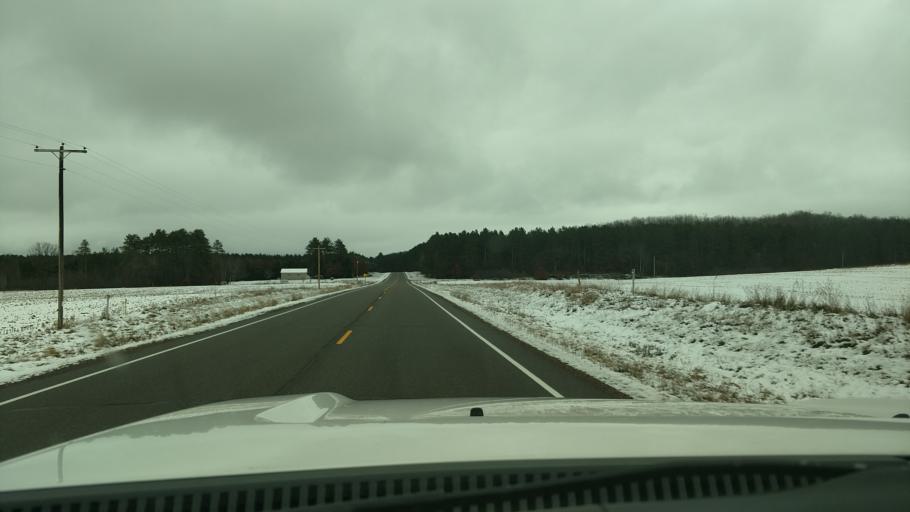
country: US
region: Wisconsin
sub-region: Dunn County
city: Colfax
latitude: 45.1390
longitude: -91.7517
